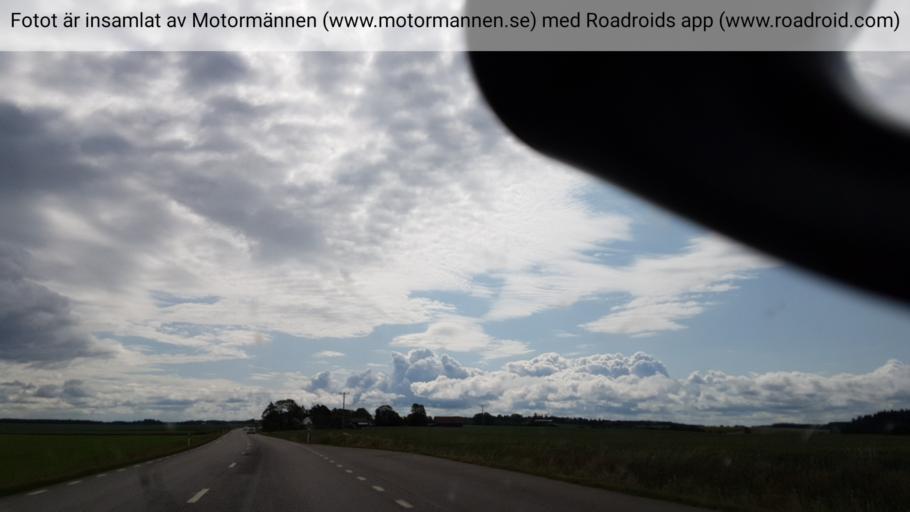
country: SE
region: Vaestra Goetaland
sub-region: Vara Kommun
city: Kvanum
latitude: 58.2309
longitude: 13.1420
